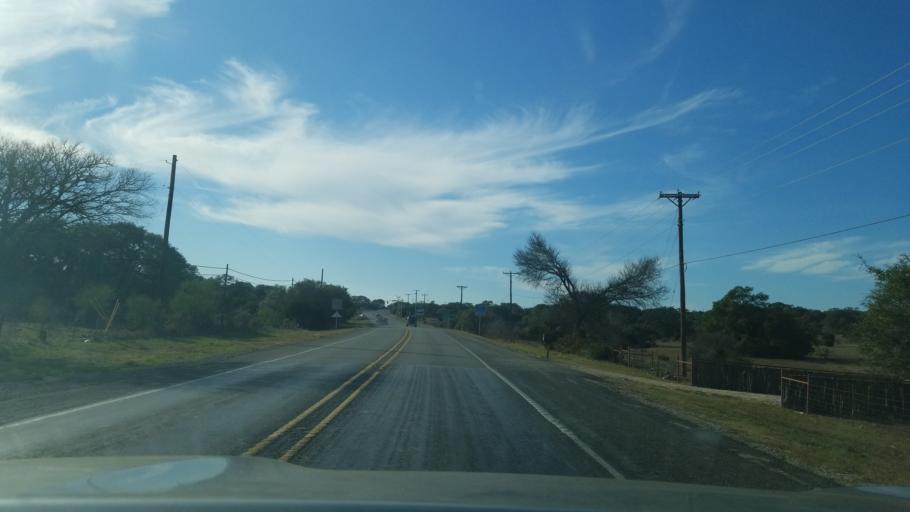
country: US
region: Texas
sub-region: Comal County
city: Canyon Lake
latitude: 29.7737
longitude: -98.2941
